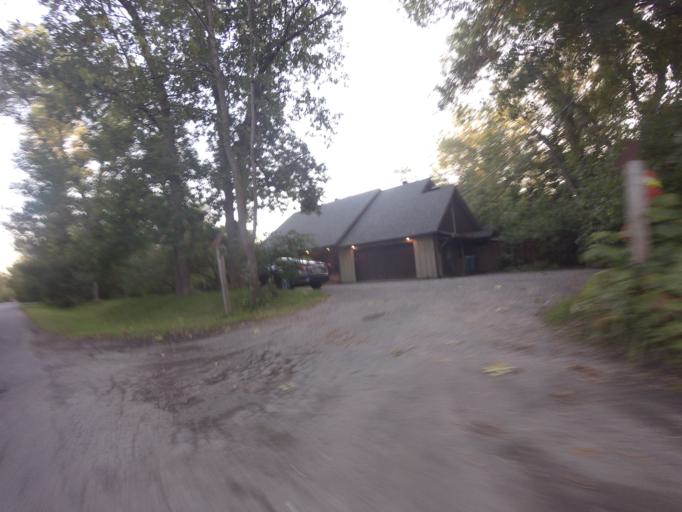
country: CA
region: Quebec
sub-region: Laurentides
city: Oka
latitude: 45.4453
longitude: -74.1070
